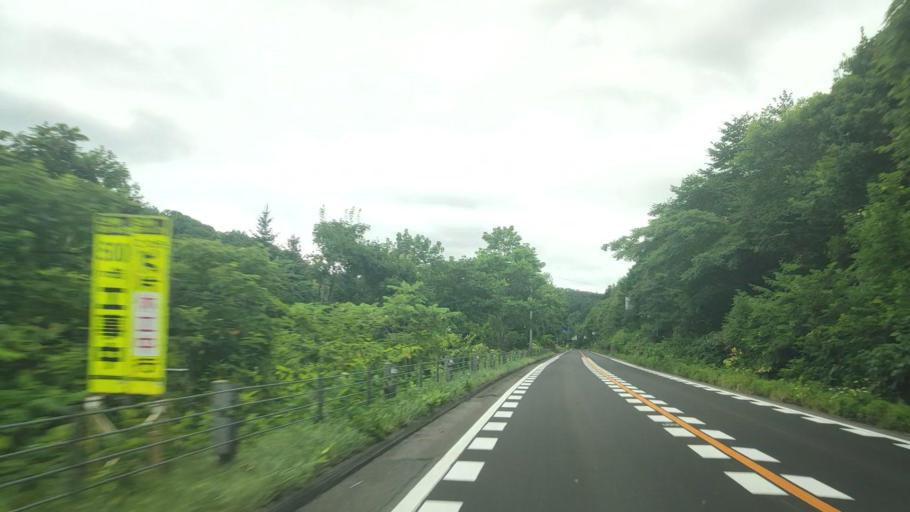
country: JP
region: Hokkaido
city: Niseko Town
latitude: 42.5992
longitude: 140.6065
